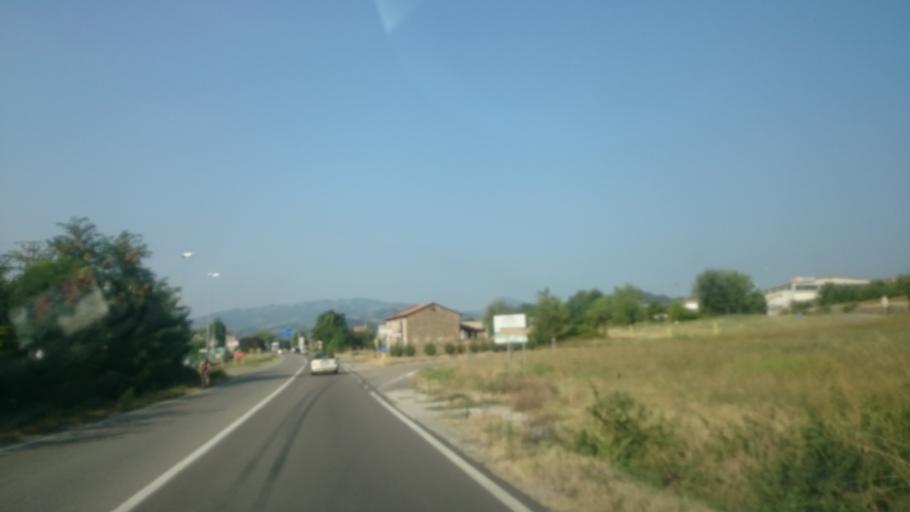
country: IT
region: Emilia-Romagna
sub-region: Provincia di Reggio Emilia
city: Roteglia
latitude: 44.4914
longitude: 10.7001
